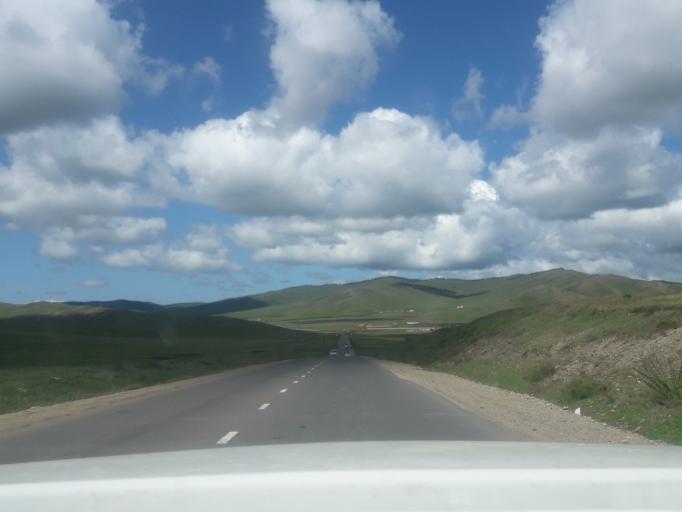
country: MN
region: Central Aimak
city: Ihsueuej
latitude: 48.1591
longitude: 106.4053
